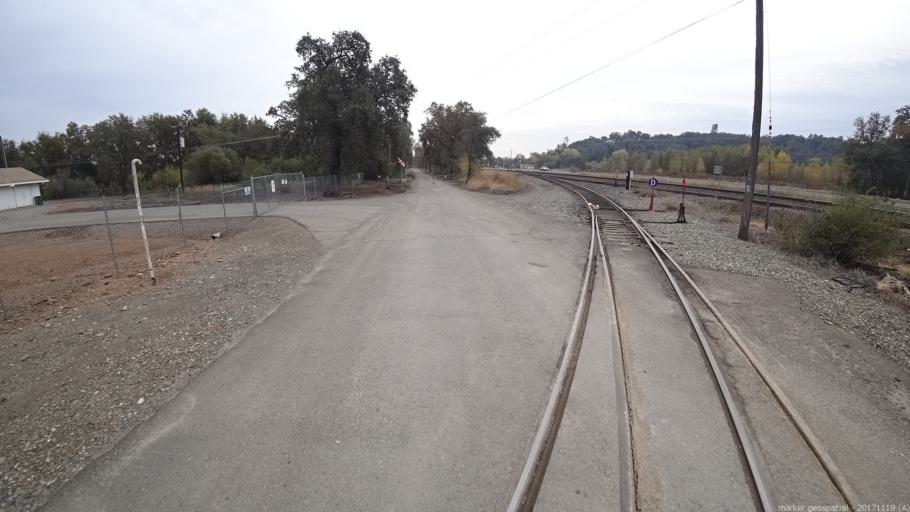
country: US
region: California
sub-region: Shasta County
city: Anderson
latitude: 40.4801
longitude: -122.3437
